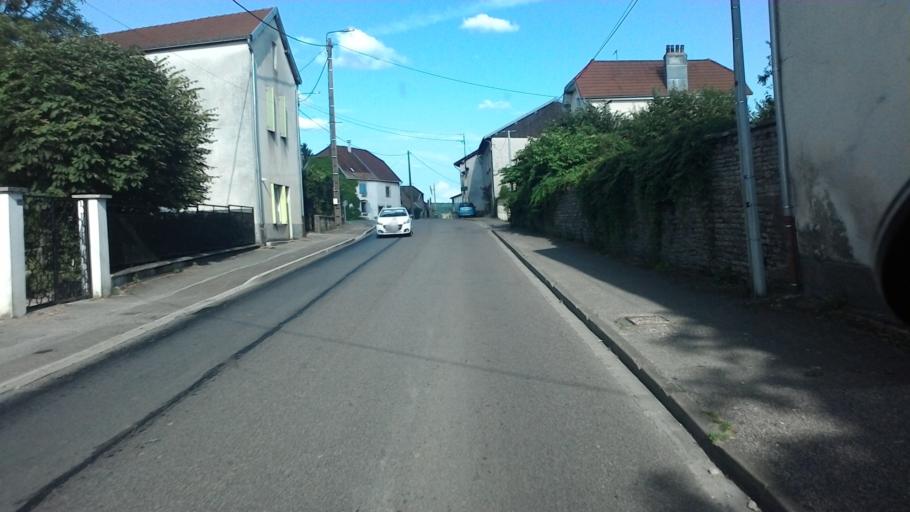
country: FR
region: Franche-Comte
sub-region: Departement de la Haute-Saone
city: Frotey-les-Vesoul
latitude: 47.6954
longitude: 6.2826
